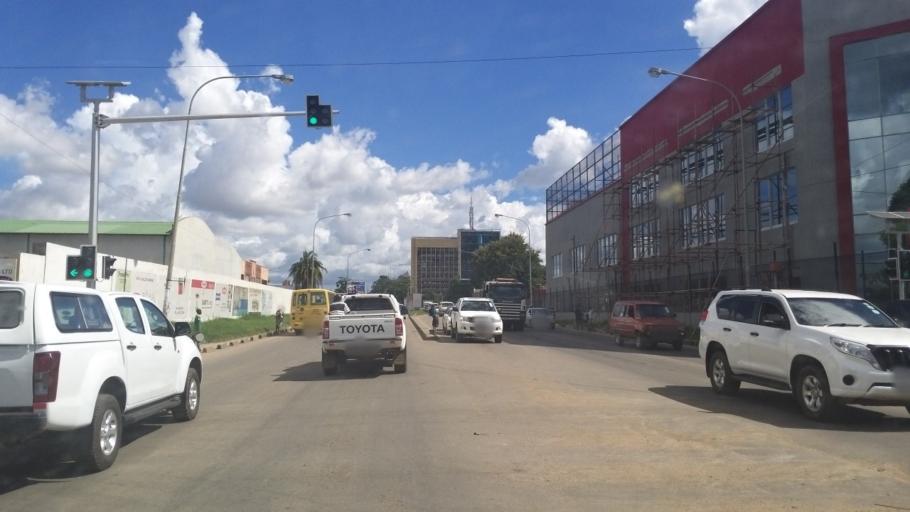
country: ZM
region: Lusaka
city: Lusaka
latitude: -15.4047
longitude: 28.2792
